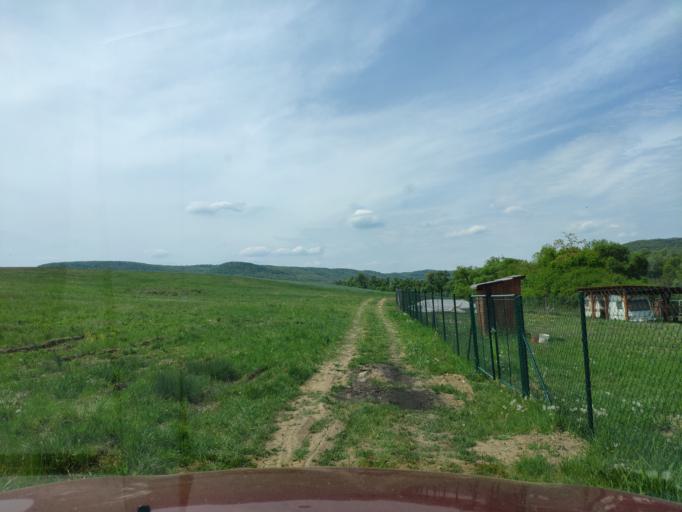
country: SK
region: Banskobystricky
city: Rimavska Sobota
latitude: 48.4769
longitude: 20.0820
